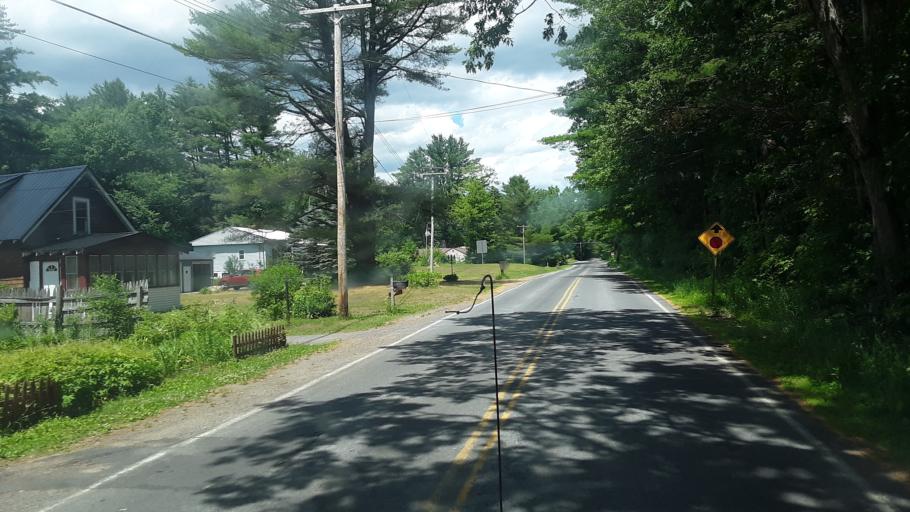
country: US
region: New York
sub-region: Oneida County
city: Rome
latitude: 43.2500
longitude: -75.5968
